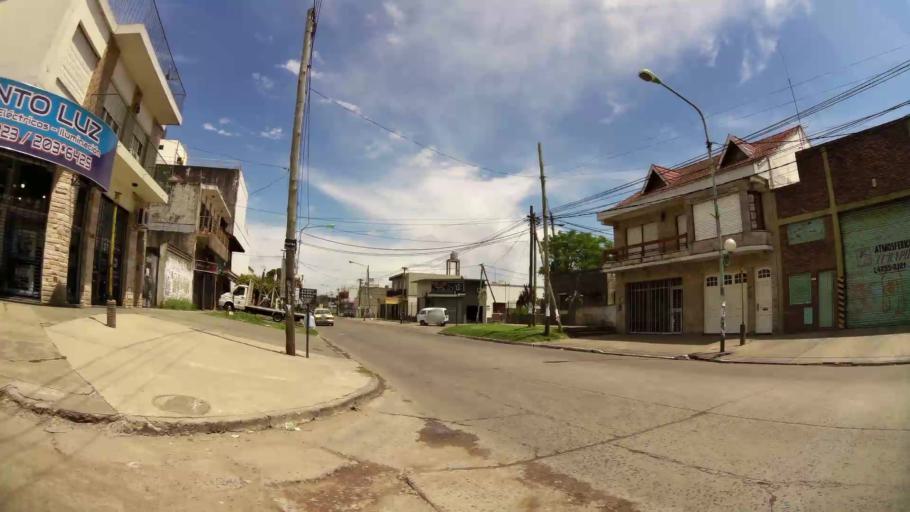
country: AR
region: Buenos Aires
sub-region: Partido de Quilmes
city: Quilmes
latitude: -34.7837
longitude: -58.2678
